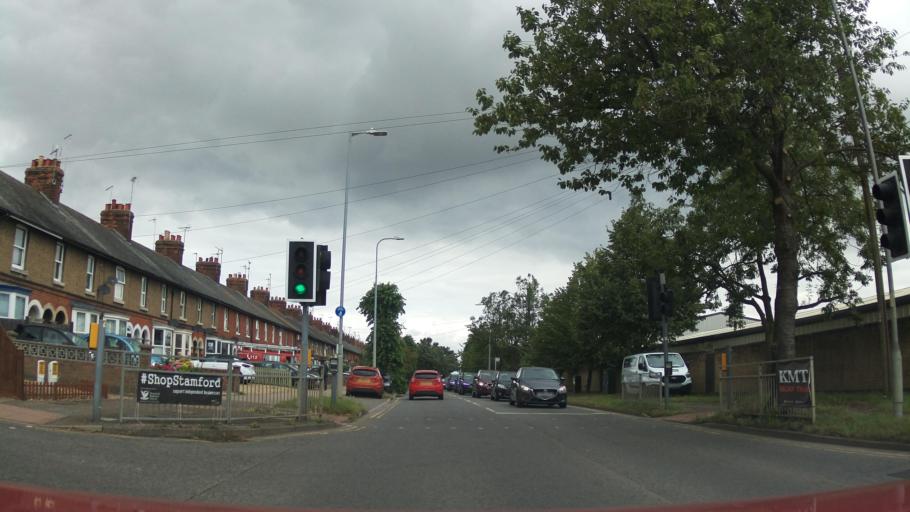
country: GB
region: England
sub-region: Lincolnshire
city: Stamford
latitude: 52.6595
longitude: -0.4660
